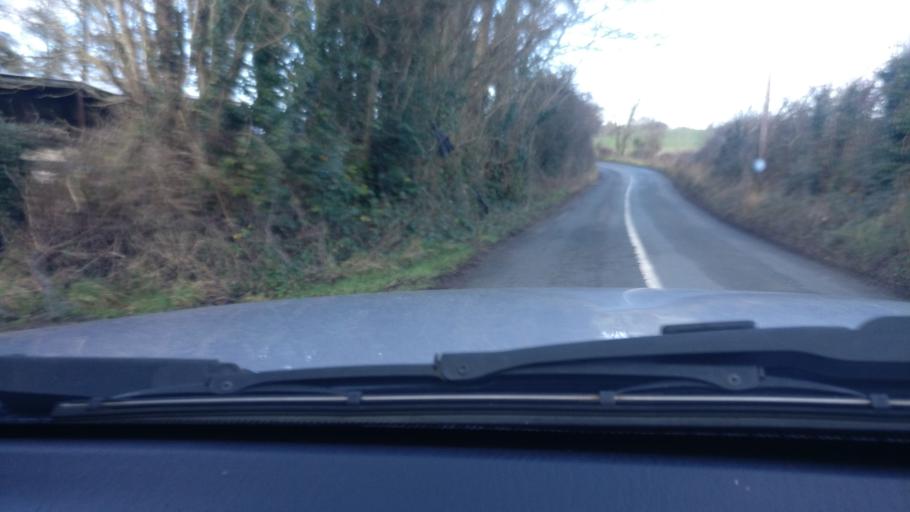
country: IE
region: Connaught
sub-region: County Galway
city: Ballinasloe
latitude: 53.2241
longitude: -8.2915
